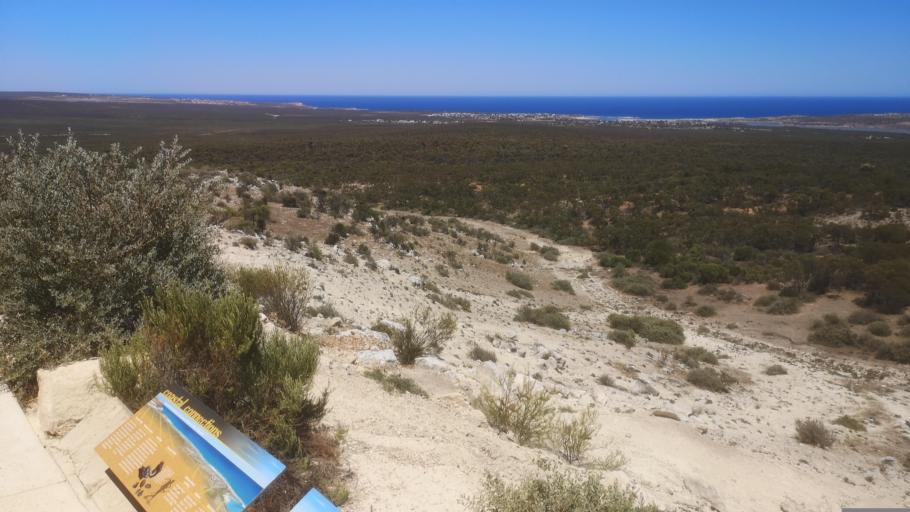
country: AU
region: Western Australia
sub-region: Northampton Shire
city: Kalbarri
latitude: -27.6984
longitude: 114.2159
